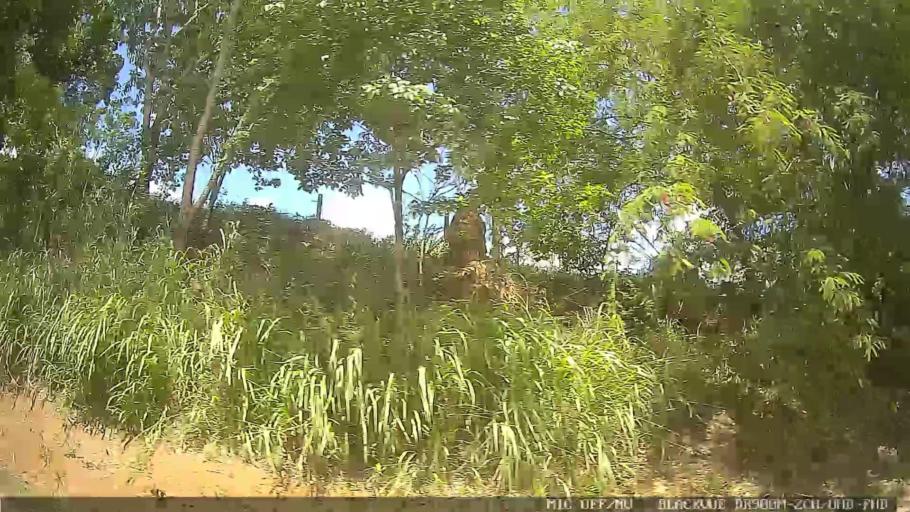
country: BR
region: Sao Paulo
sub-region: Conchas
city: Conchas
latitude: -23.0204
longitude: -48.0177
